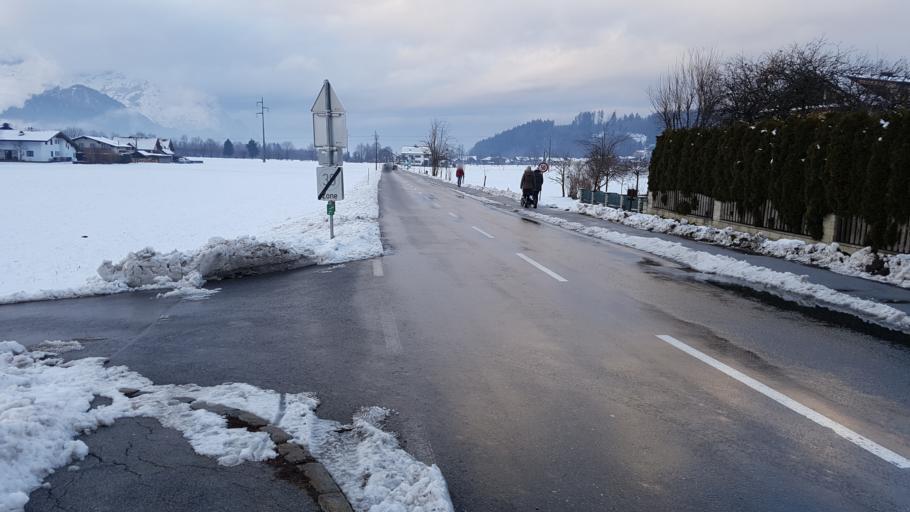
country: AT
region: Salzburg
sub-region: Politischer Bezirk Hallein
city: Adnet
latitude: 47.6672
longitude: 13.1331
